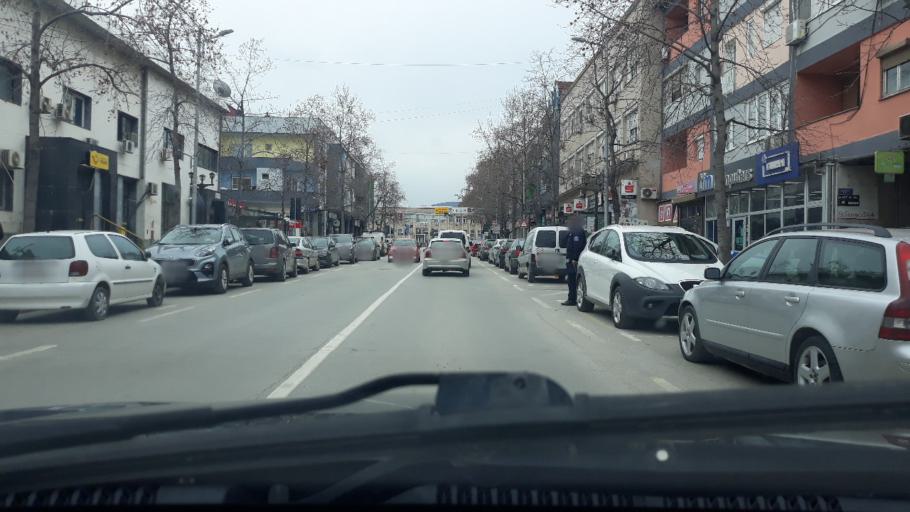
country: MK
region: Kavadarci
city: Kavadarci
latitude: 41.4349
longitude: 22.0114
